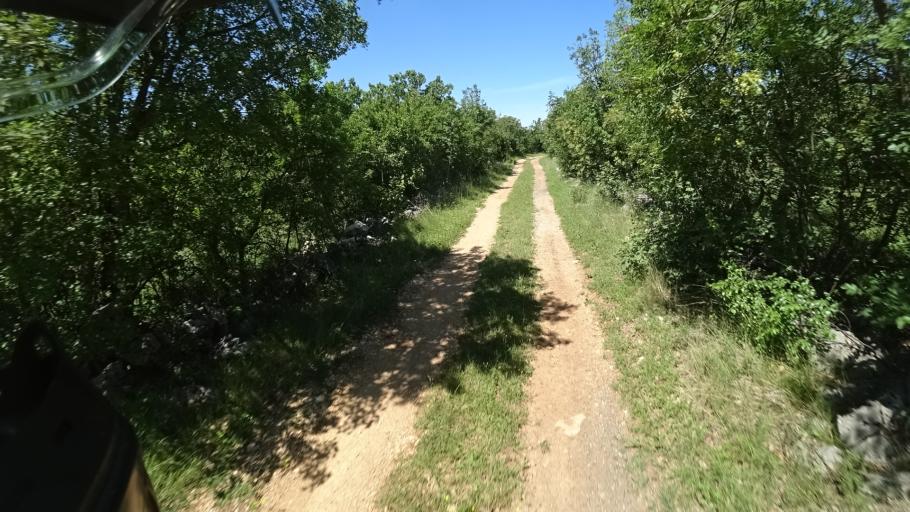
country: BA
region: Federation of Bosnia and Herzegovina
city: Bosansko Grahovo
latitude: 43.9942
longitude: 16.4166
